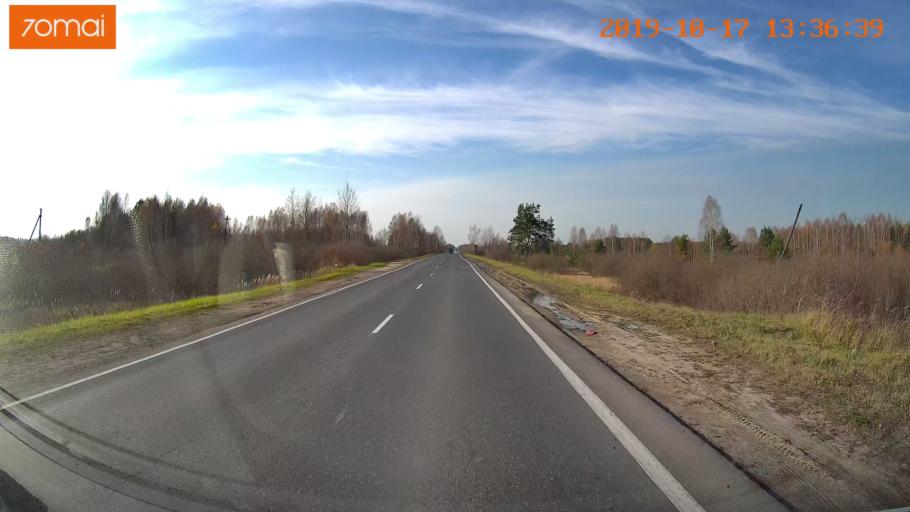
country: RU
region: Rjazan
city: Tuma
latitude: 55.1398
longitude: 40.6585
